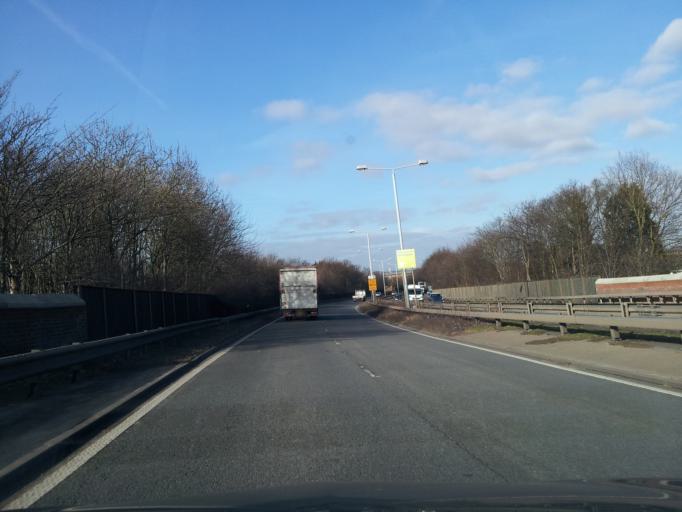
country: GB
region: England
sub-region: Nottinghamshire
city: Ruddington
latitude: 52.9129
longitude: -1.1586
